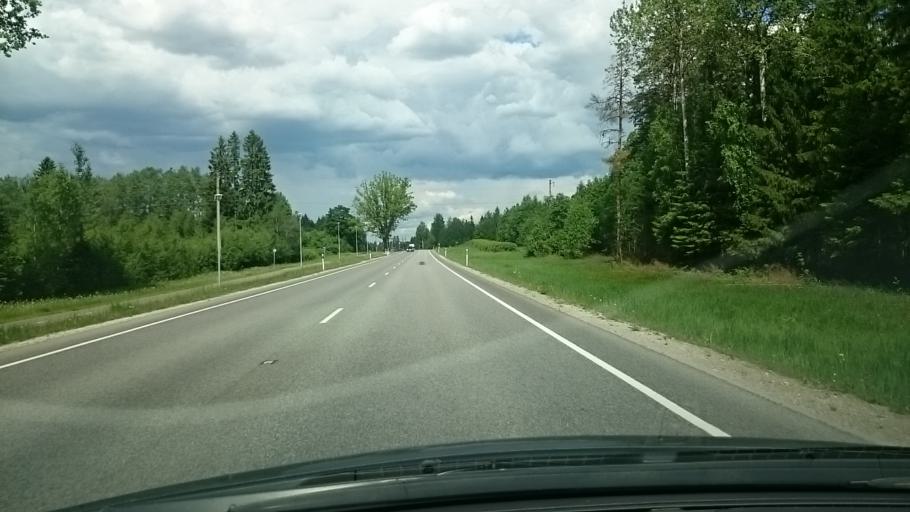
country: EE
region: Jaervamaa
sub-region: Paide linn
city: Paide
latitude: 58.8646
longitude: 25.4922
